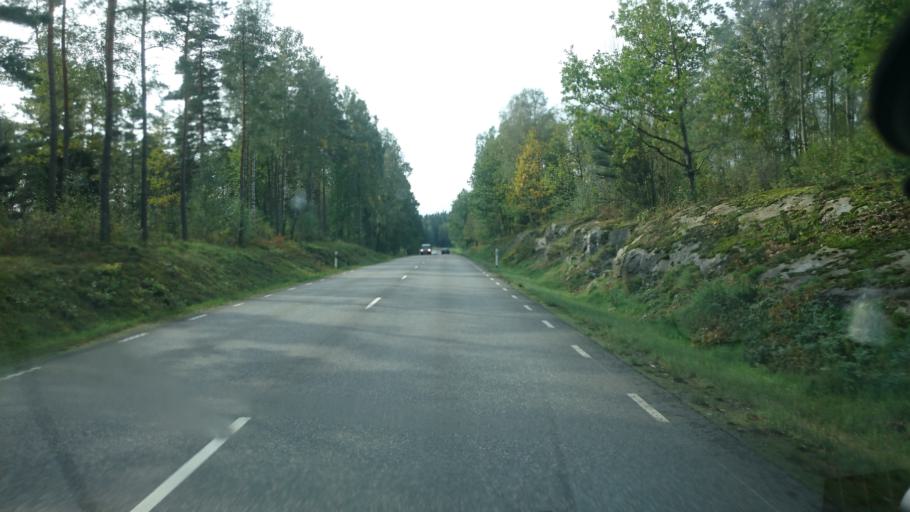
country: SE
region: Vaestra Goetaland
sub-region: Alingsas Kommun
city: Alingsas
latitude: 58.0119
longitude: 12.4487
